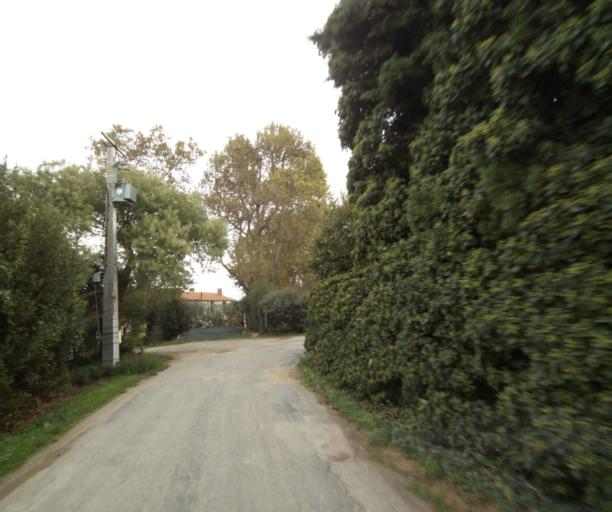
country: FR
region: Languedoc-Roussillon
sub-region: Departement des Pyrenees-Orientales
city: Latour-Bas-Elne
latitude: 42.5855
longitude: 3.0174
